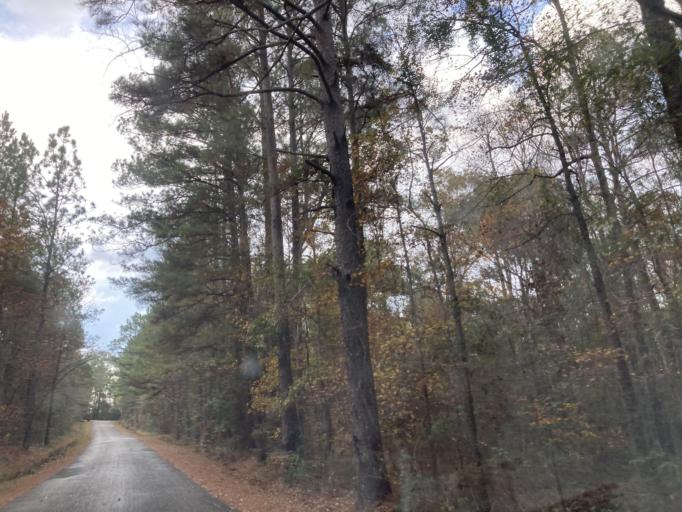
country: US
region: Mississippi
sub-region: Marion County
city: Columbia
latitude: 31.1880
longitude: -89.6466
